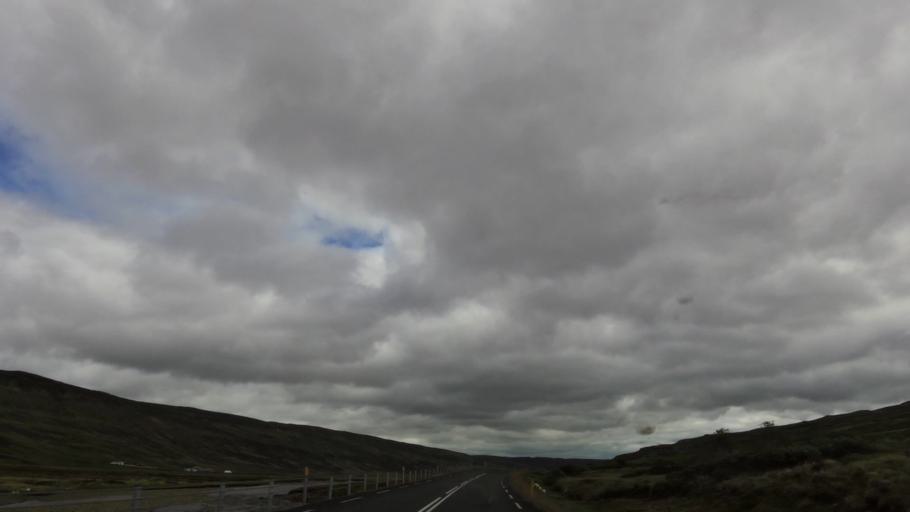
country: IS
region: West
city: Stykkisholmur
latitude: 65.7589
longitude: -21.8575
